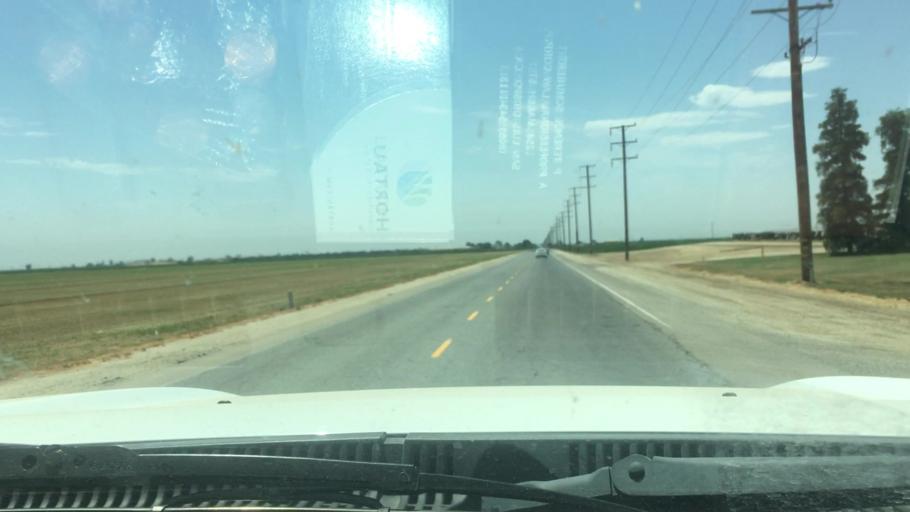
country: US
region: California
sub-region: Tulare County
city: Tipton
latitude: 36.0657
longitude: -119.2706
